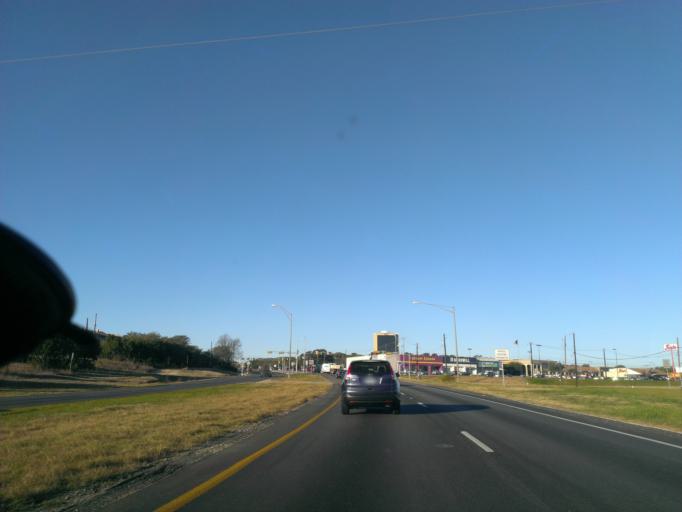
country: US
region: Texas
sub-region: Travis County
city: Barton Creek
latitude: 30.2339
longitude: -97.8729
